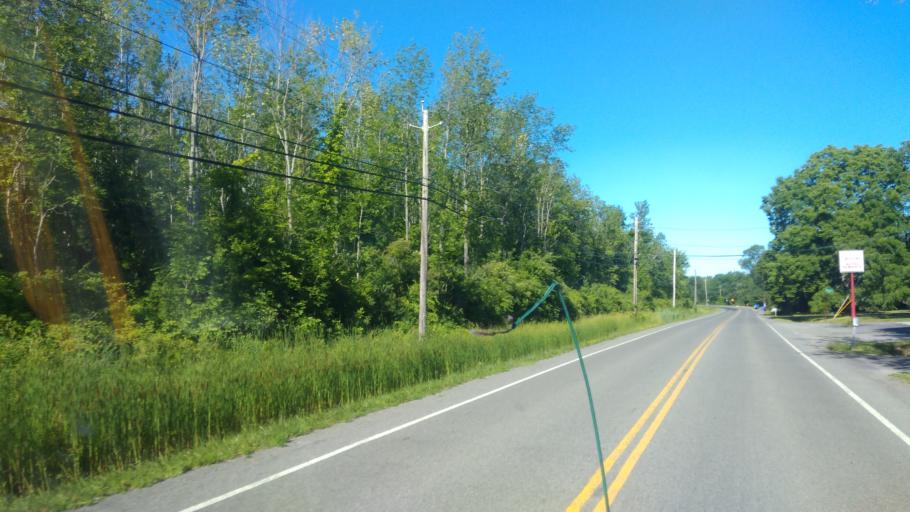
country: US
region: New York
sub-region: Monroe County
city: Webster
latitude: 43.2700
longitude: -77.3712
